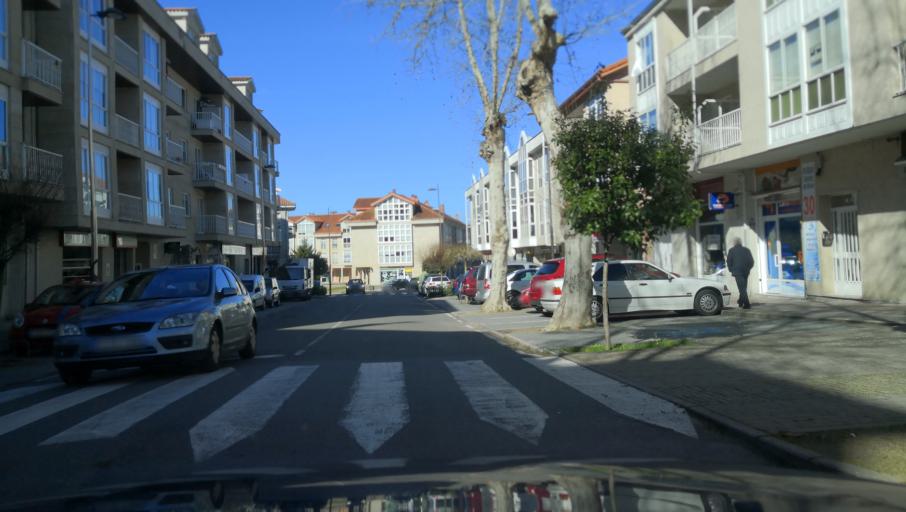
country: ES
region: Galicia
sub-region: Provincia de Ourense
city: Allariz
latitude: 42.1874
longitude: -7.7984
